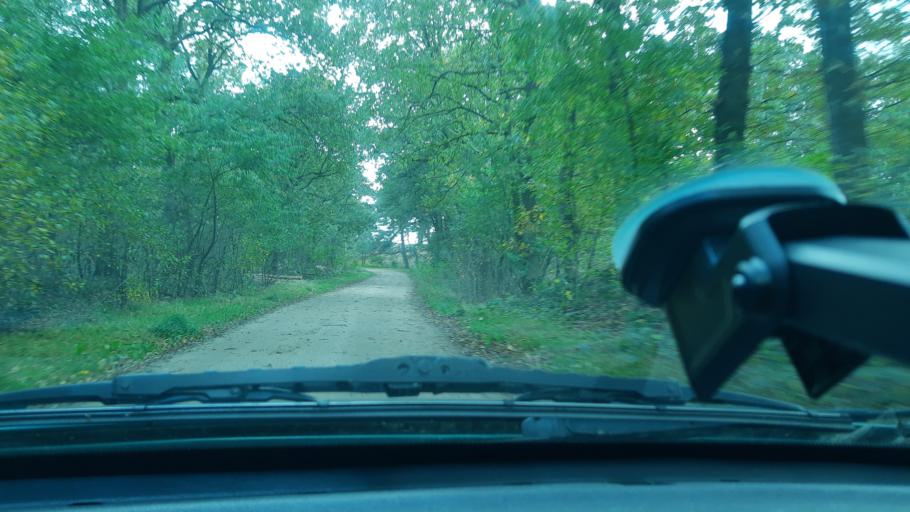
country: NL
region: Limburg
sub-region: Gemeente Gennep
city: Gennep
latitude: 51.6544
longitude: 6.0064
